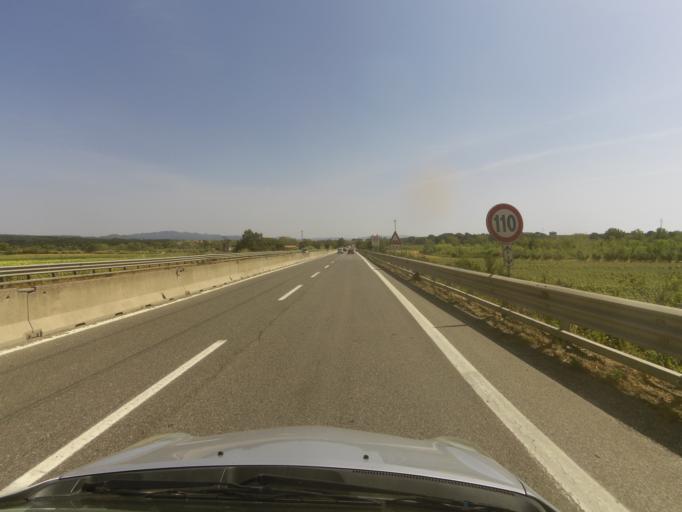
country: IT
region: Tuscany
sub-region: Provincia di Livorno
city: S.P. in Palazzi
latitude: 43.3284
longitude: 10.5277
